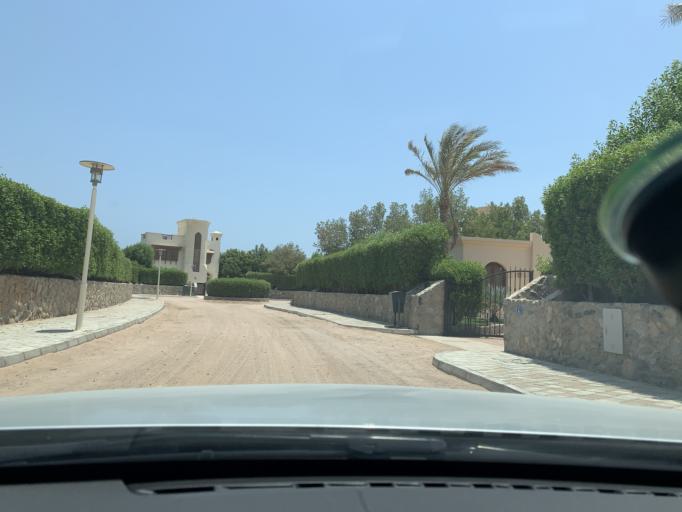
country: EG
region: Red Sea
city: El Gouna
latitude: 27.4140
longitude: 33.6699
